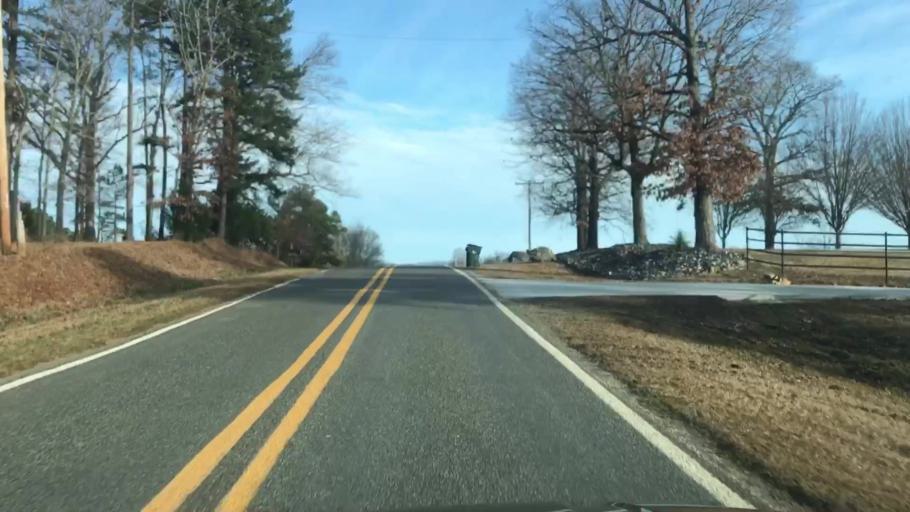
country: US
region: Arkansas
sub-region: Garland County
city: Rockwell
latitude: 34.5024
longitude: -93.2762
